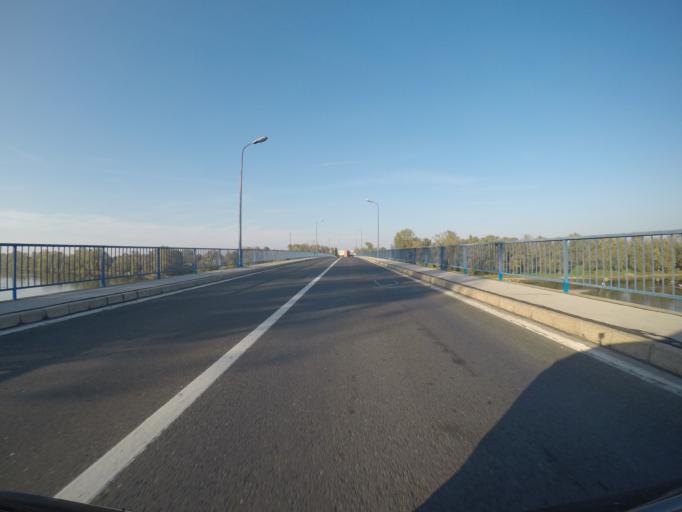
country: HU
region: Somogy
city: Barcs
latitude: 45.9446
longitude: 17.4615
